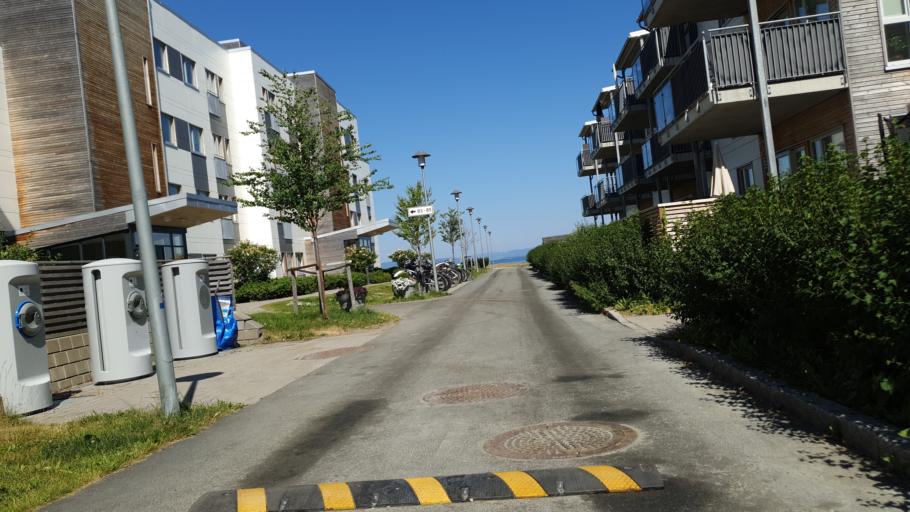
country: NO
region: Sor-Trondelag
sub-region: Trondheim
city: Trondheim
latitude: 63.4297
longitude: 10.5272
